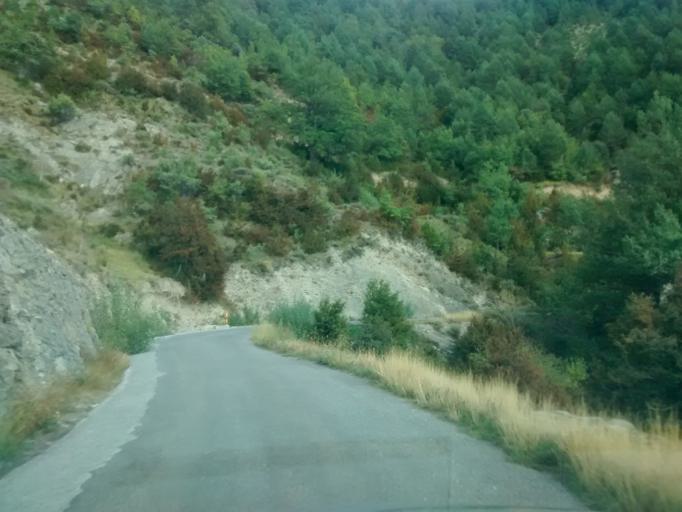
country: ES
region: Aragon
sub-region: Provincia de Huesca
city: Puertolas
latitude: 42.5862
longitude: 0.1704
